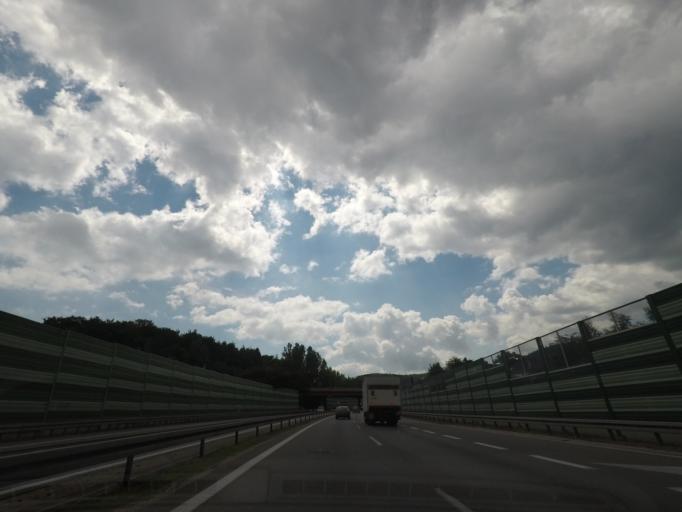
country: PL
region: Pomeranian Voivodeship
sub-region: Gdynia
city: Pogorze
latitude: 54.5362
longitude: 18.4549
